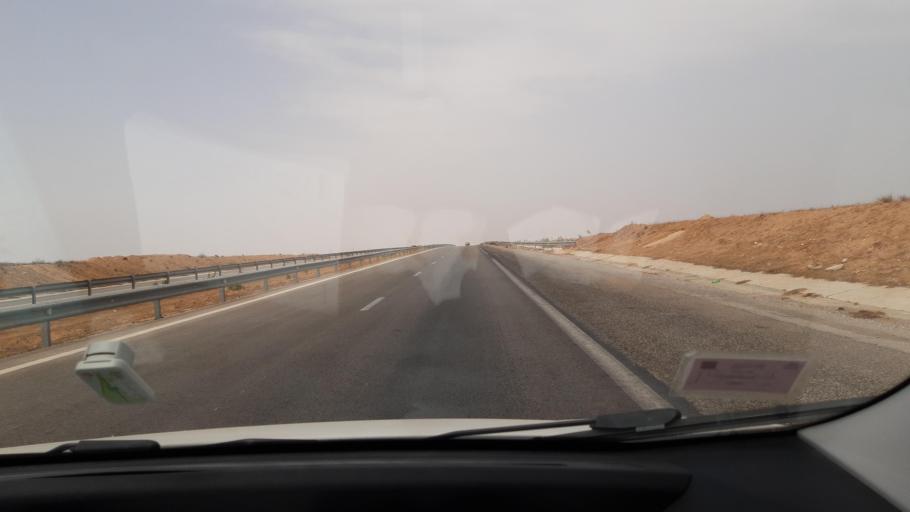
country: TN
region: Safaqis
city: Sfax
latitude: 34.7593
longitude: 10.6077
